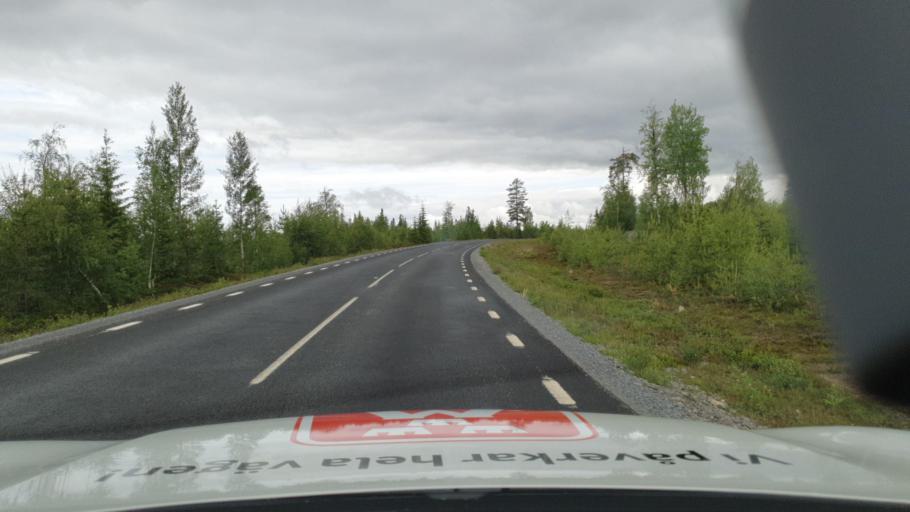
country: SE
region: Vaesterbotten
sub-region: Dorotea Kommun
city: Dorotea
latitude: 64.1949
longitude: 16.5820
